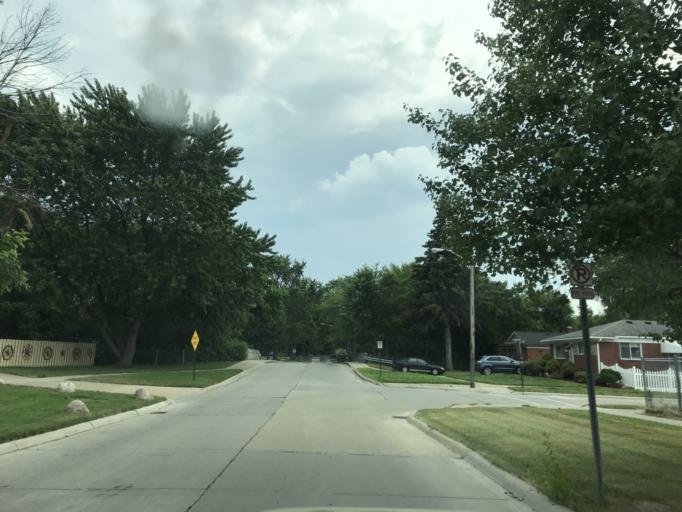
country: US
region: Michigan
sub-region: Wayne County
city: Taylor
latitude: 42.2731
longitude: -83.2654
